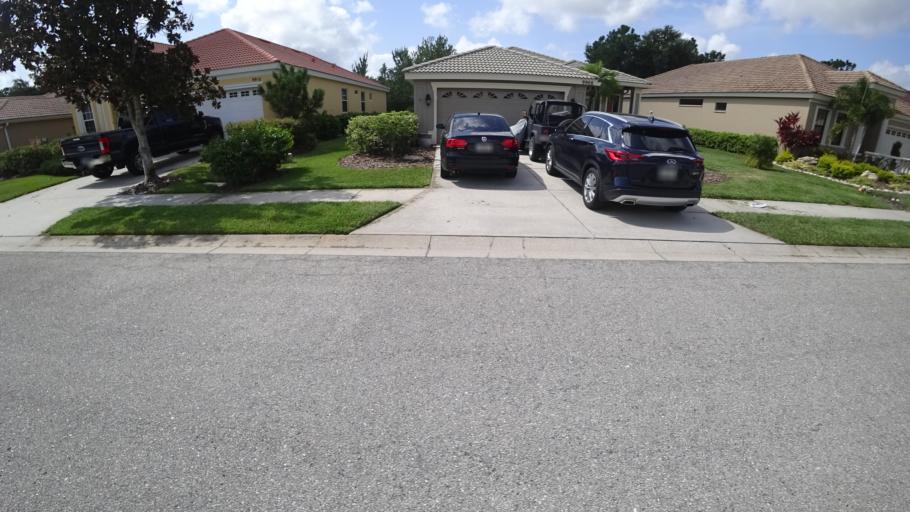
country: US
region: Florida
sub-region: Sarasota County
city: The Meadows
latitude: 27.4101
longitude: -82.4411
